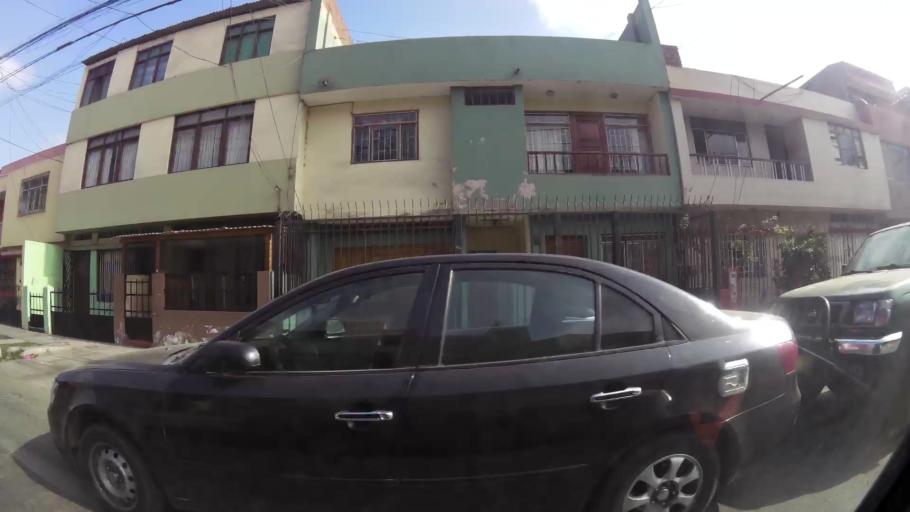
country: PE
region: La Libertad
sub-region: Provincia de Trujillo
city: Trujillo
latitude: -8.1086
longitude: -79.0134
